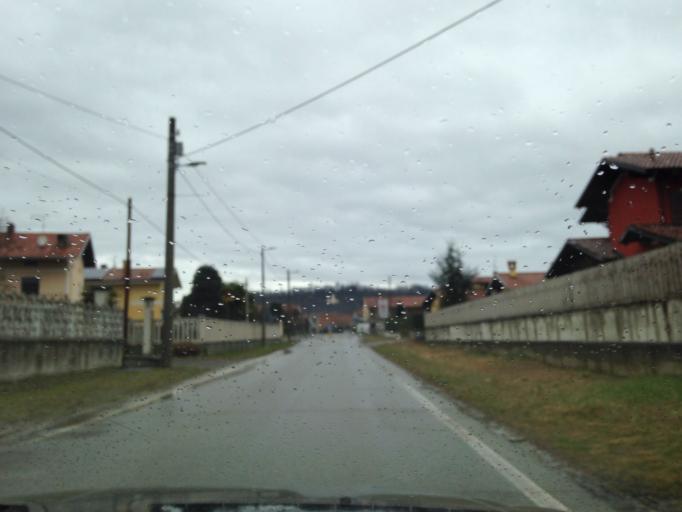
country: IT
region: Piedmont
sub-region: Provincia di Torino
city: Villareggia
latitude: 45.3071
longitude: 7.9774
